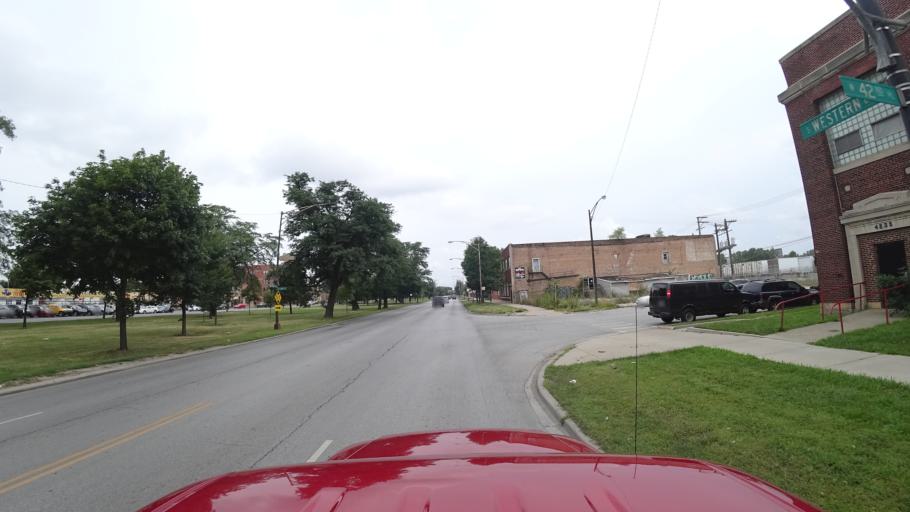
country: US
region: Illinois
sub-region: Cook County
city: Chicago
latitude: 41.8163
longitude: -87.6840
